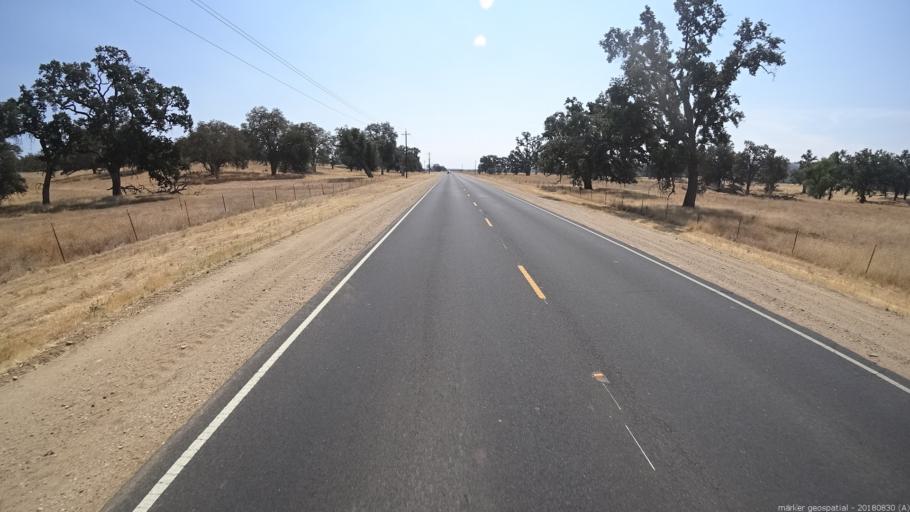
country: US
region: California
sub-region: Monterey County
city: King City
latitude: 35.9759
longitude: -121.2110
